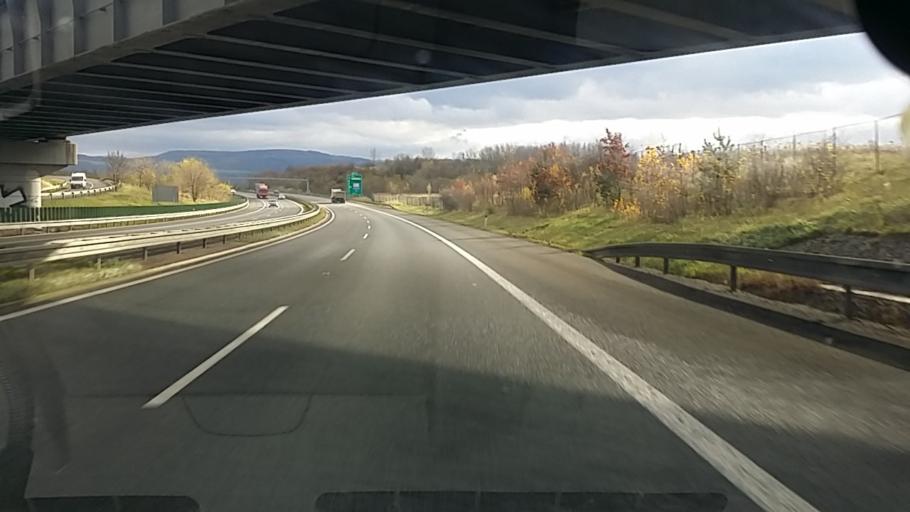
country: CZ
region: Ustecky
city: Chabarovice
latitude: 50.6758
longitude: 13.9626
